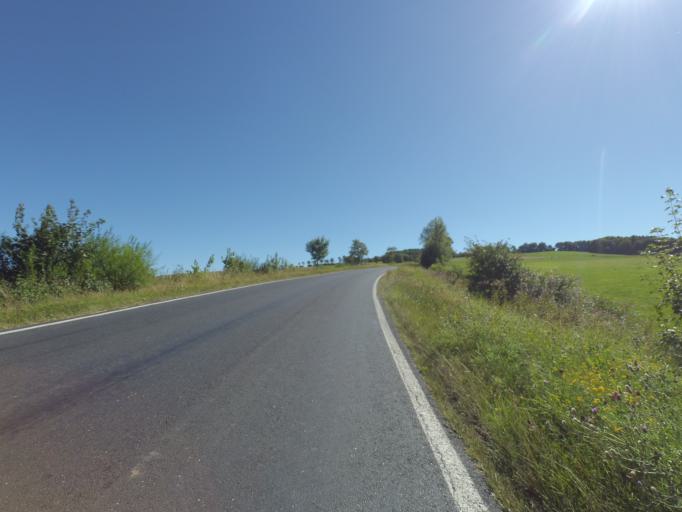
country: DE
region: Rheinland-Pfalz
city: Bongard
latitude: 50.2953
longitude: 6.8079
